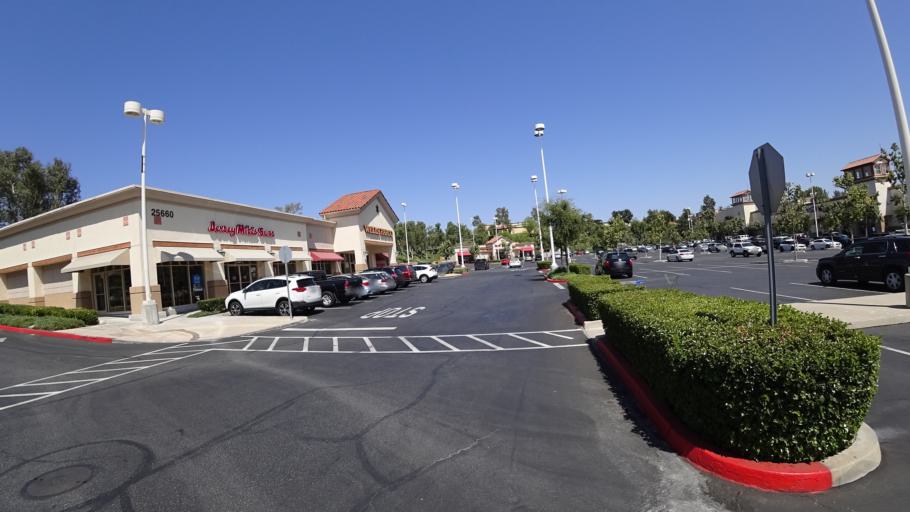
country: US
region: California
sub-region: Los Angeles County
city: Santa Clarita
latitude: 34.3877
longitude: -118.5720
